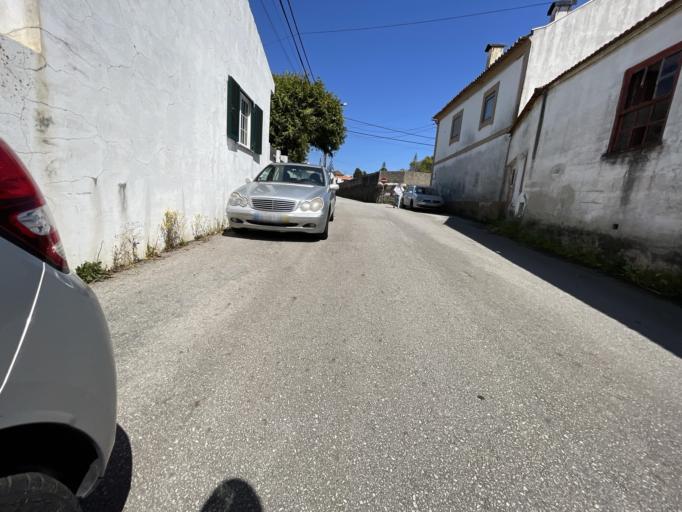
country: PT
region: Aveiro
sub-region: Ovar
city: Cortegaca
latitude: 40.9474
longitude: -8.6251
